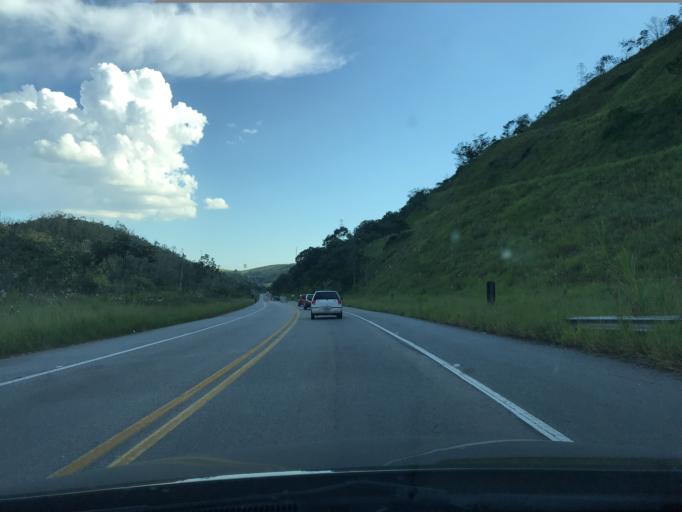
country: BR
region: Sao Paulo
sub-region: Tremembe
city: Tremembe
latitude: -22.8773
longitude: -45.5981
